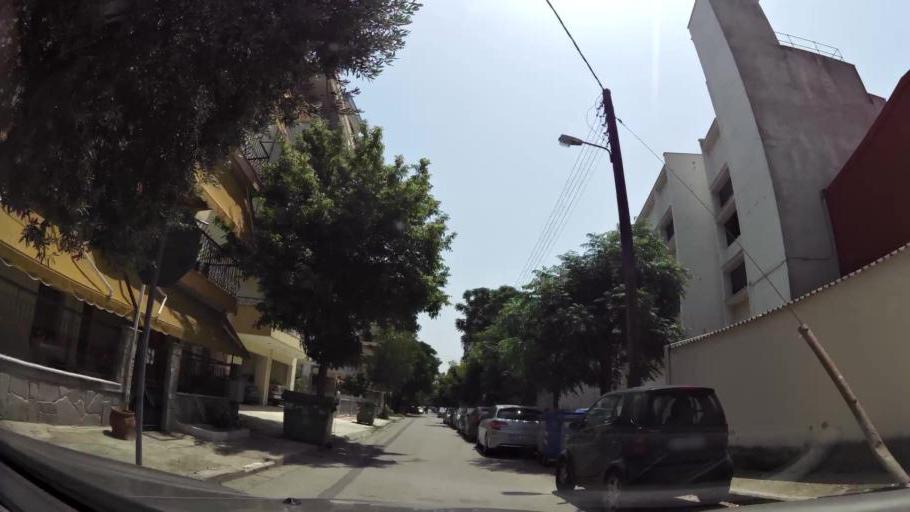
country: GR
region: Central Macedonia
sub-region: Nomos Thessalonikis
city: Menemeni
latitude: 40.6692
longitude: 22.8881
